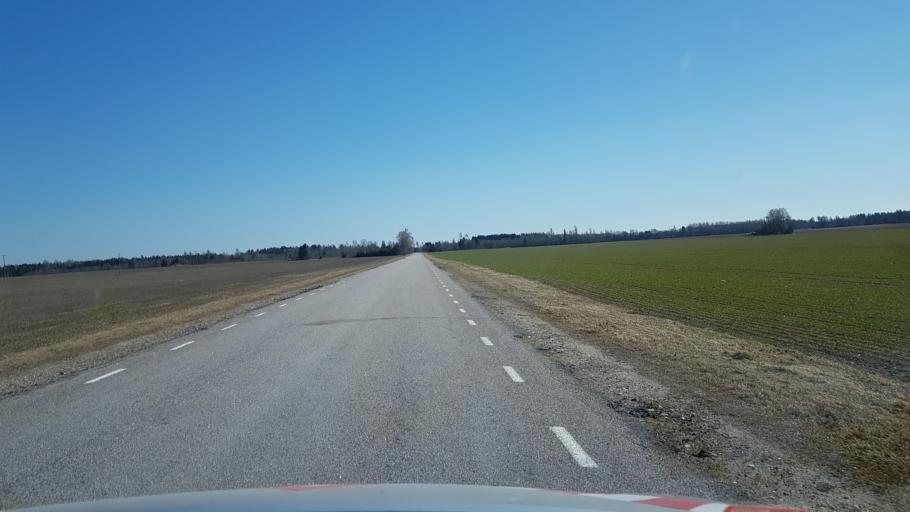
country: EE
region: Laeaene-Virumaa
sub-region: Vaeike-Maarja vald
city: Vaike-Maarja
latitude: 59.1048
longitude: 26.3875
